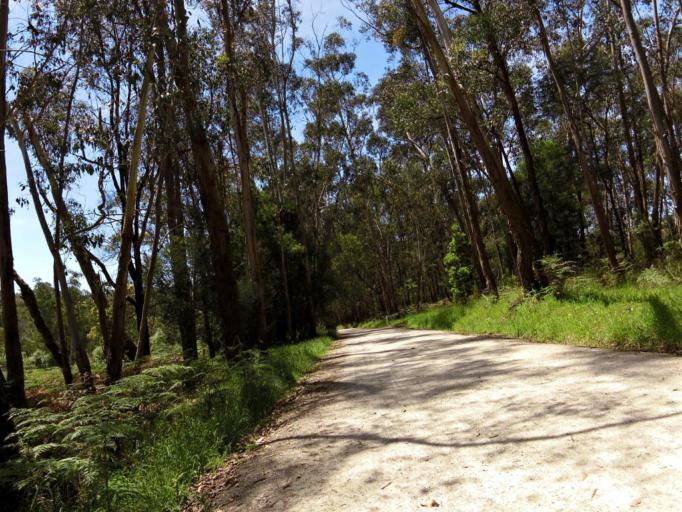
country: AU
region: Victoria
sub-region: Yarra Ranges
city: Woori Yallock
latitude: -37.7638
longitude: 145.4635
